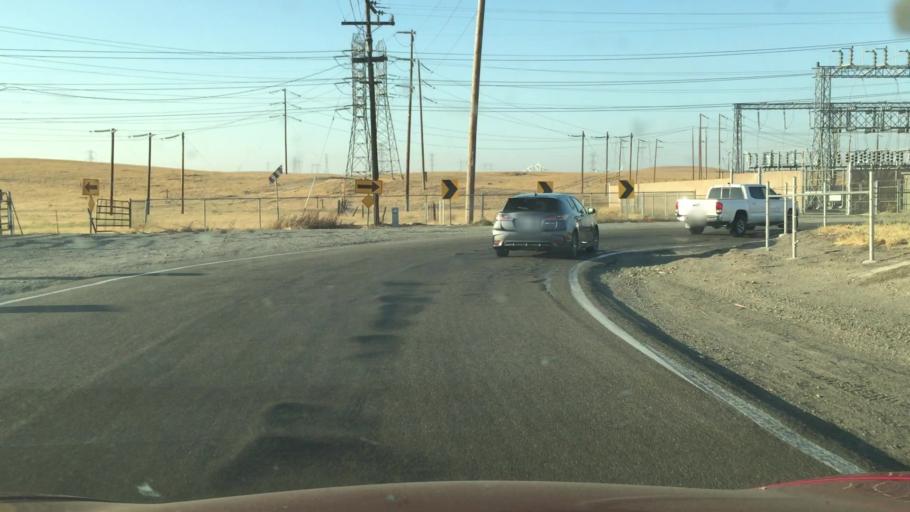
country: US
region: California
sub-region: San Joaquin County
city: Mountain House
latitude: 37.7147
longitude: -121.5680
